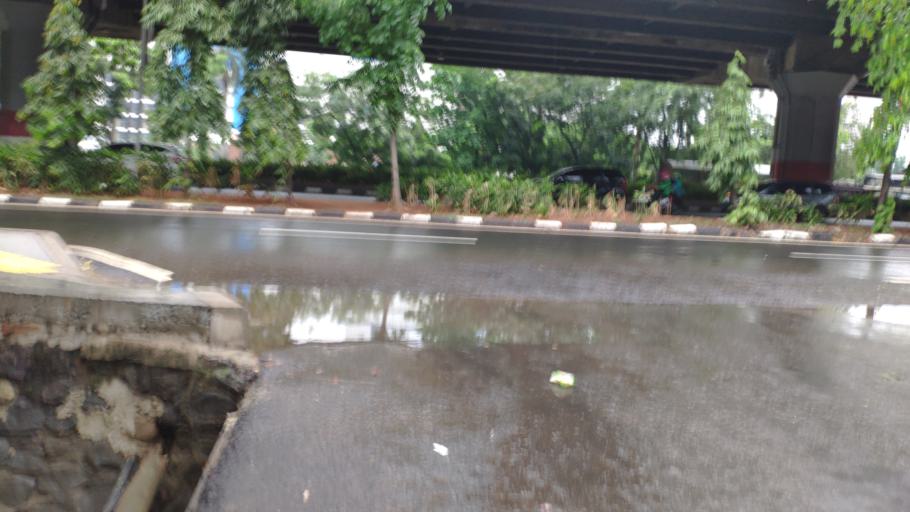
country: ID
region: Jakarta Raya
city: Jakarta
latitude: -6.2066
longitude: 106.8735
